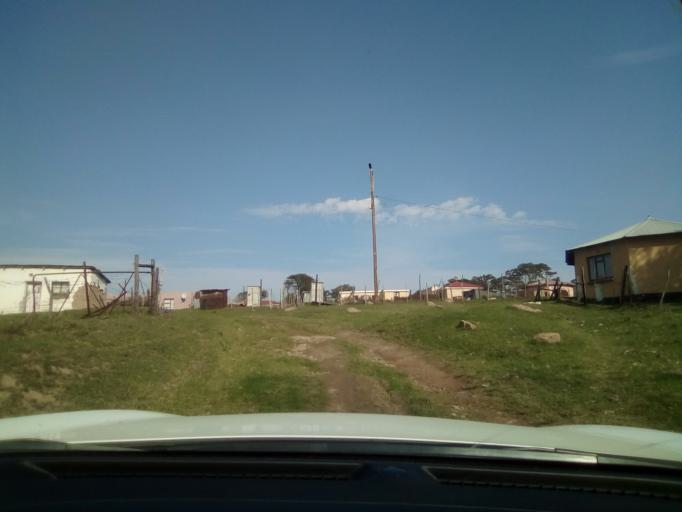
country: ZA
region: Eastern Cape
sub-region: Buffalo City Metropolitan Municipality
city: Bhisho
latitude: -32.9832
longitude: 27.2620
